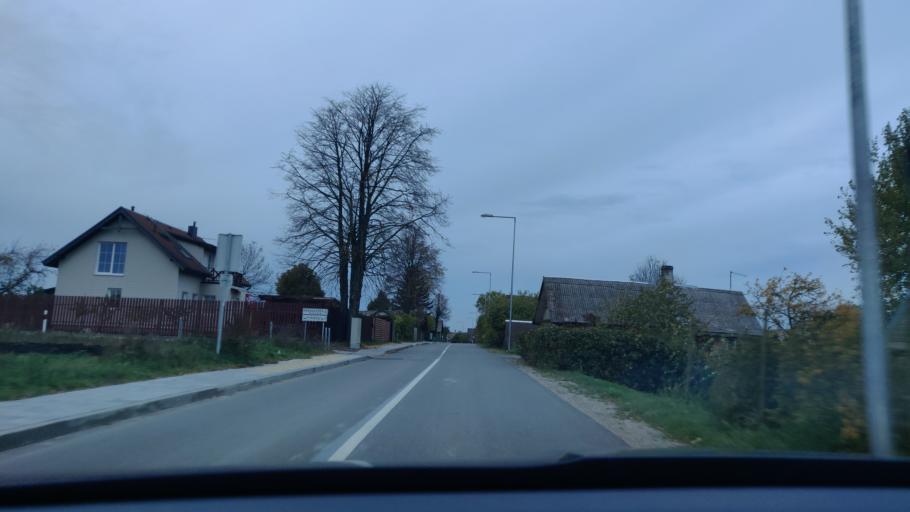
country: LT
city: Lentvaris
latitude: 54.5843
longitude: 25.0514
